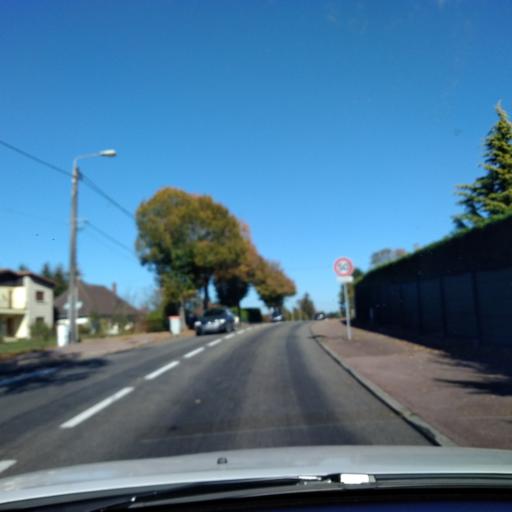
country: FR
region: Lorraine
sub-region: Departement de la Moselle
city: Neufgrange
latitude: 49.0953
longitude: 7.0437
